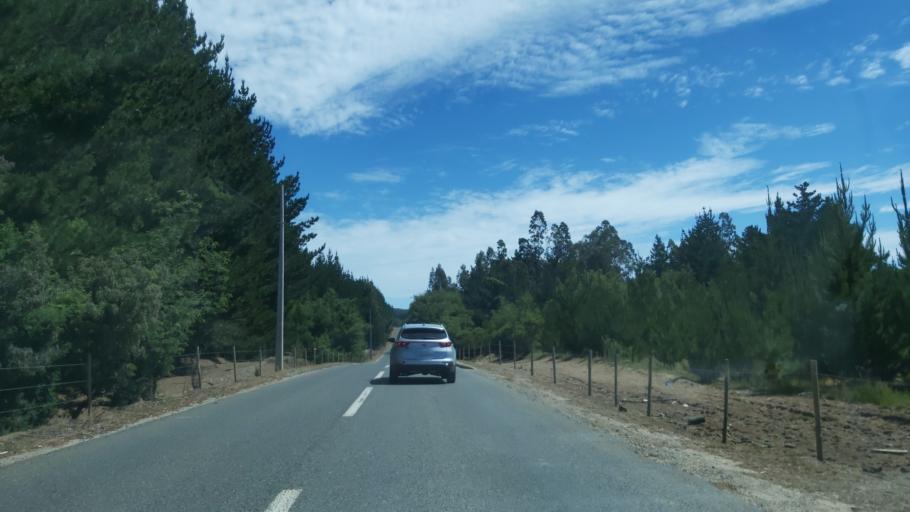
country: CL
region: Maule
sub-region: Provincia de Talca
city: Constitucion
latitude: -35.5258
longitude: -72.5384
